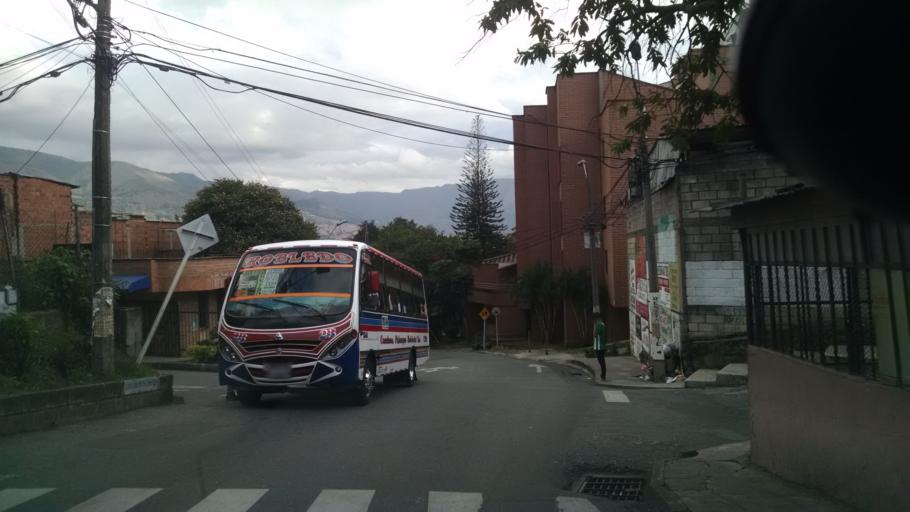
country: CO
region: Antioquia
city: Medellin
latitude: 6.2810
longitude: -75.5891
